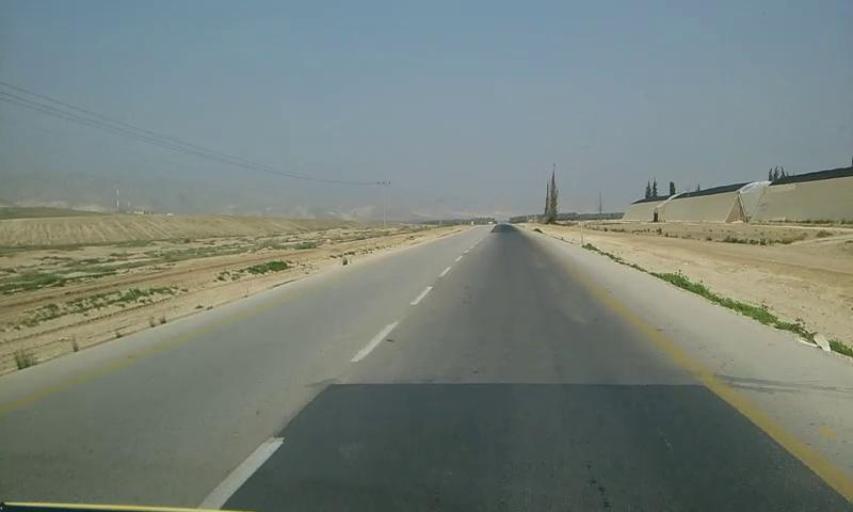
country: PS
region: West Bank
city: Al `Awja
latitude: 31.9838
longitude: 35.4637
